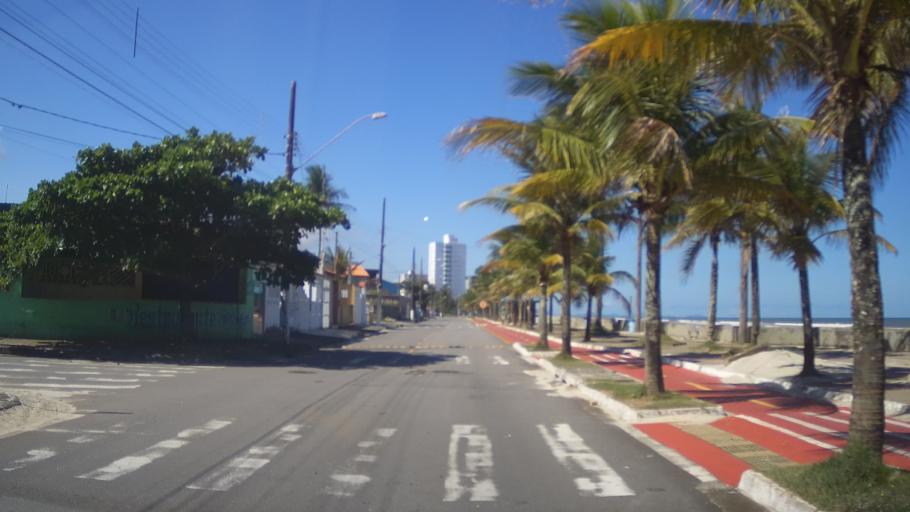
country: BR
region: Sao Paulo
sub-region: Mongagua
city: Mongagua
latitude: -24.1218
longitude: -46.6709
